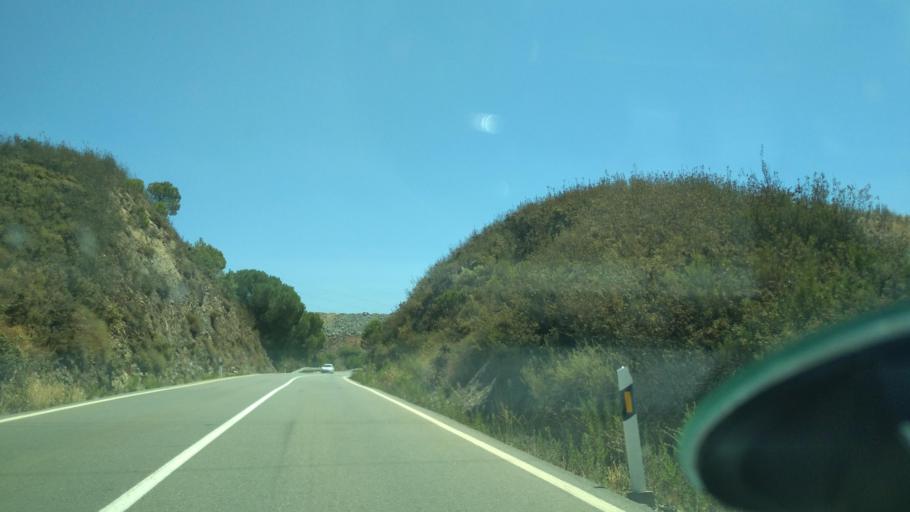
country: ES
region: Andalusia
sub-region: Provincia de Huelva
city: Nerva
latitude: 37.7213
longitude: -6.5822
